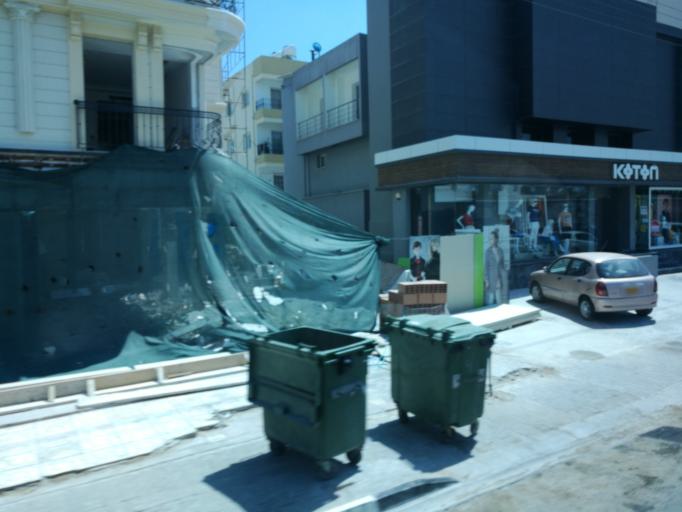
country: CY
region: Ammochostos
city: Famagusta
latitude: 35.1329
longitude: 33.9242
